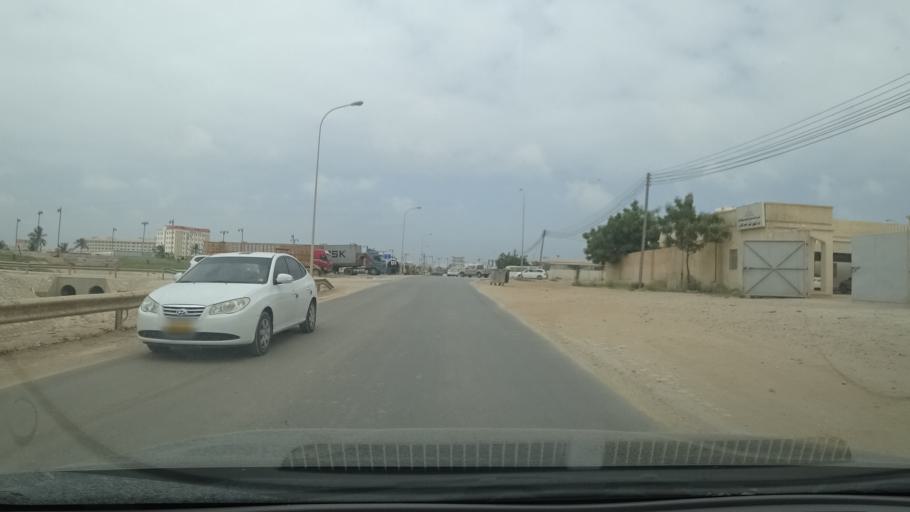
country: OM
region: Zufar
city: Salalah
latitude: 17.0224
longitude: 54.0559
